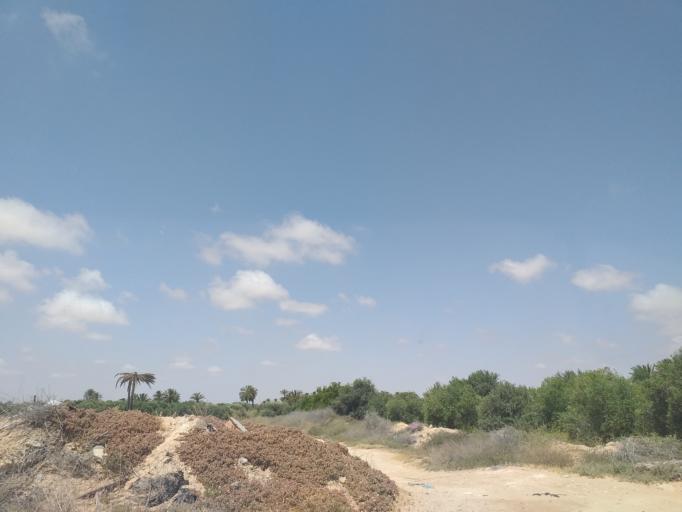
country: TN
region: Qabis
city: Gabes
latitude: 33.9492
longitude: 10.0511
